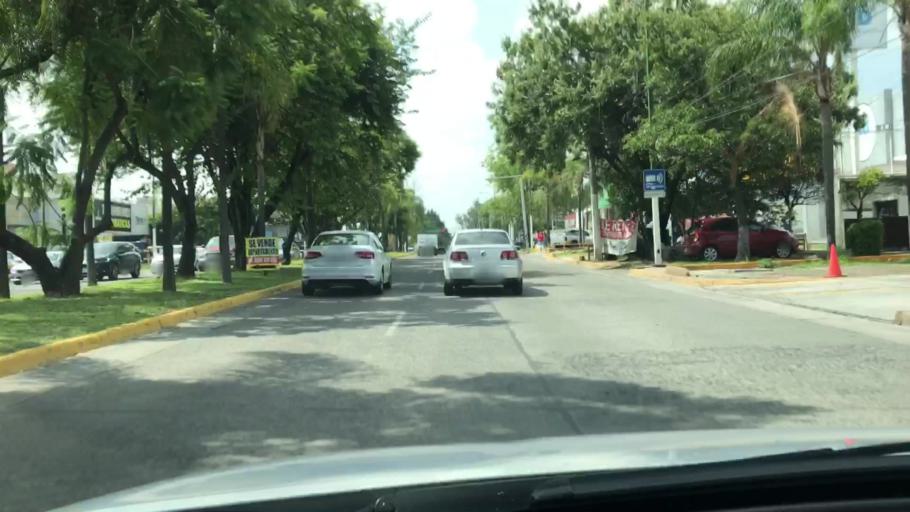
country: MX
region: Jalisco
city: Guadalajara
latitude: 20.6663
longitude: -103.4243
